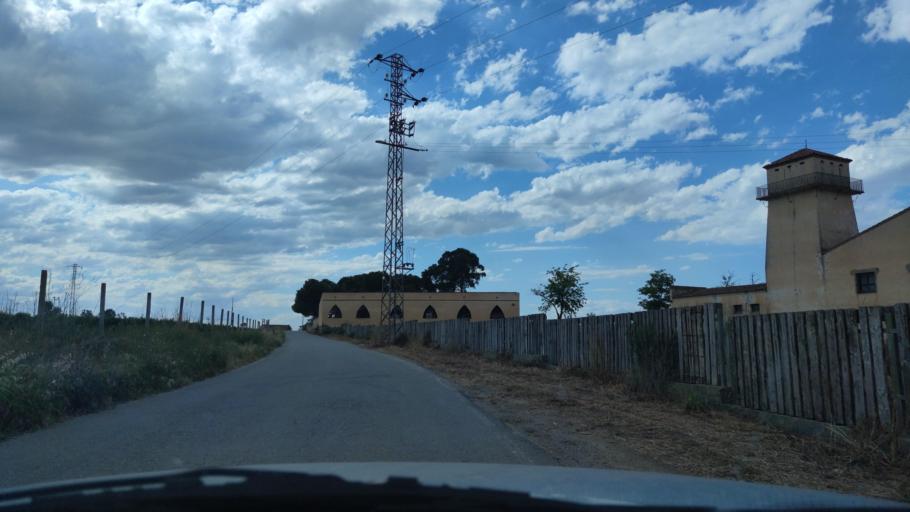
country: ES
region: Catalonia
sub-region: Provincia de Lleida
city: Alcarras
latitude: 41.5989
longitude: 0.5626
